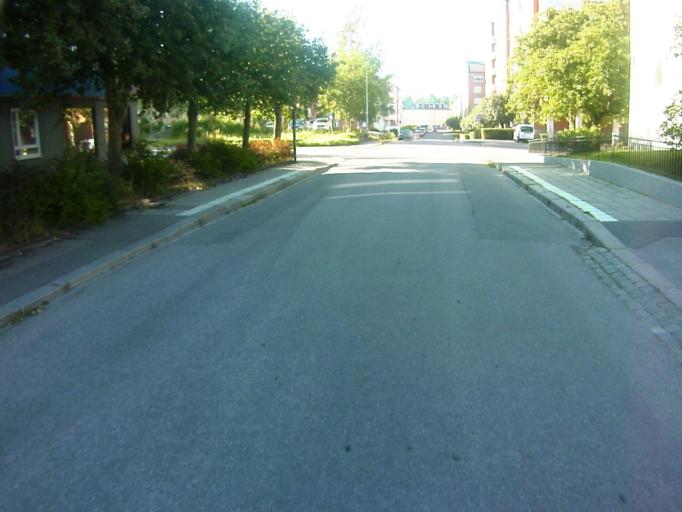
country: SE
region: Soedermanland
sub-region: Eskilstuna Kommun
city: Eskilstuna
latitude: 59.3724
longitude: 16.5227
